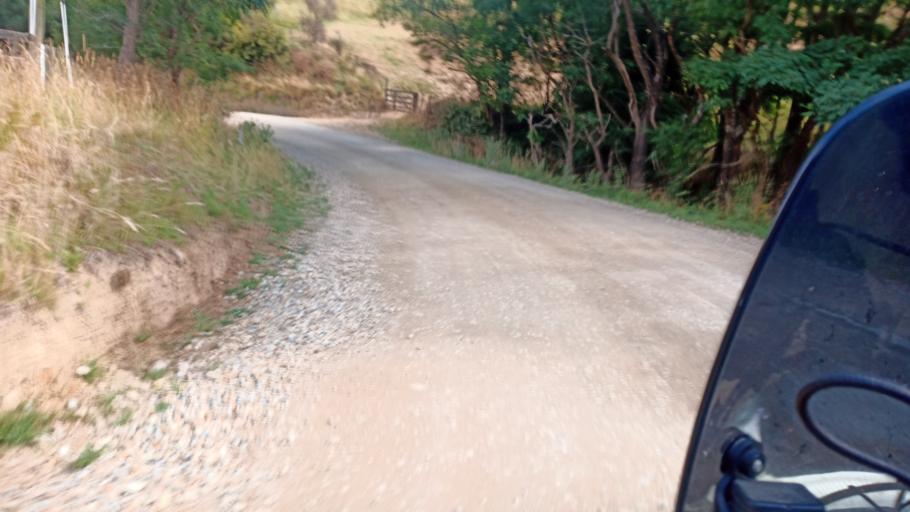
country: NZ
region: Hawke's Bay
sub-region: Wairoa District
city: Wairoa
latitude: -38.6077
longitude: 177.4602
